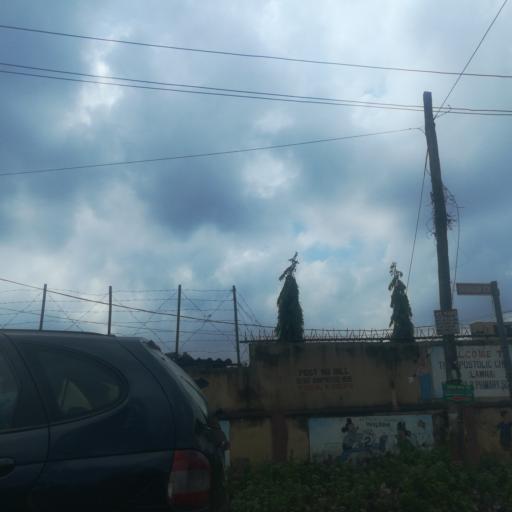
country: NG
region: Lagos
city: Ojota
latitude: 6.6020
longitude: 3.3910
